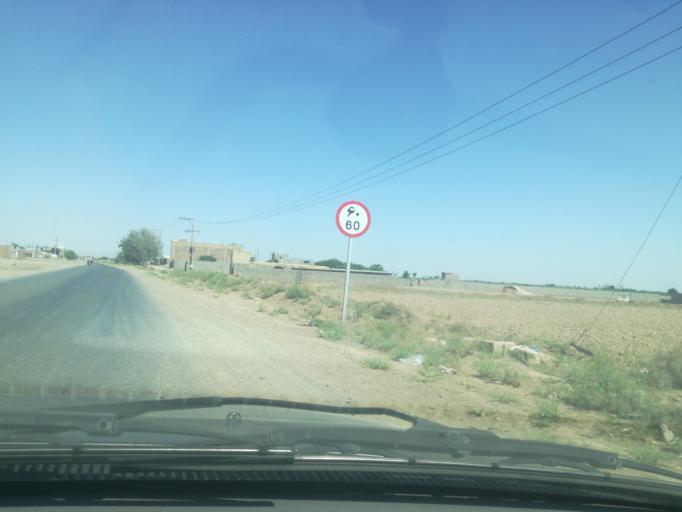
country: IR
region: Razavi Khorasan
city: Sarakhs
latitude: 36.5623
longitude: 61.1471
